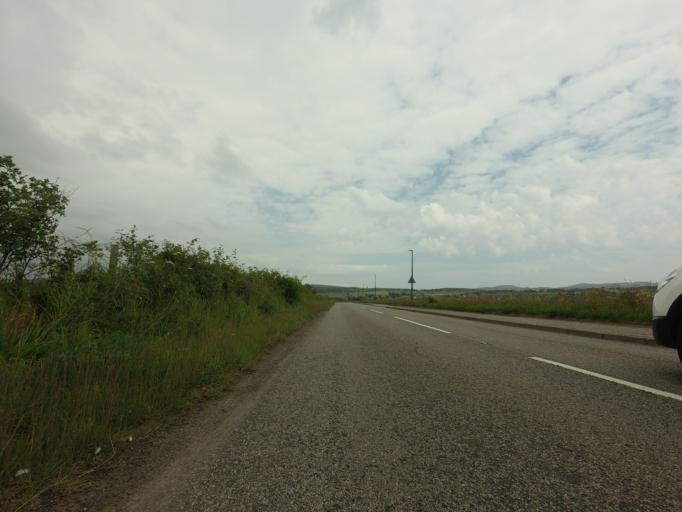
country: GB
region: Scotland
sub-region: Highland
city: Alness
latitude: 57.8852
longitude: -4.3603
